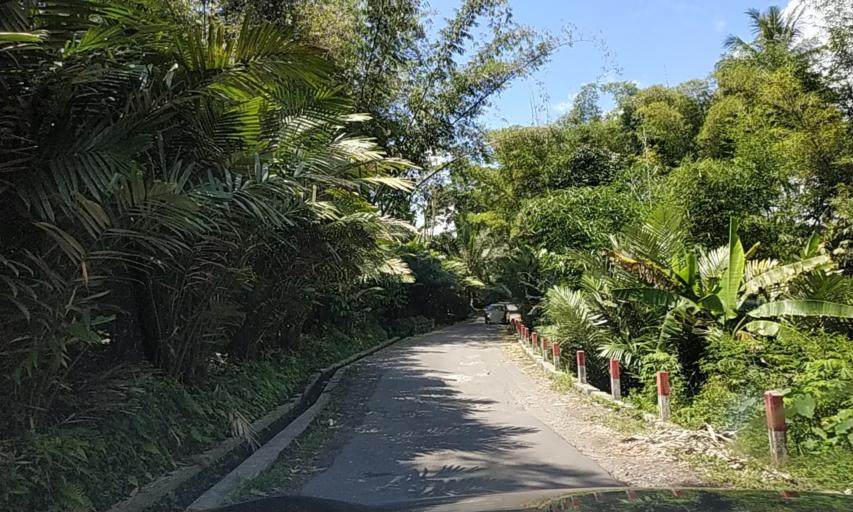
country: ID
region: Central Java
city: Muntilan
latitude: -7.5938
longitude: 110.3501
